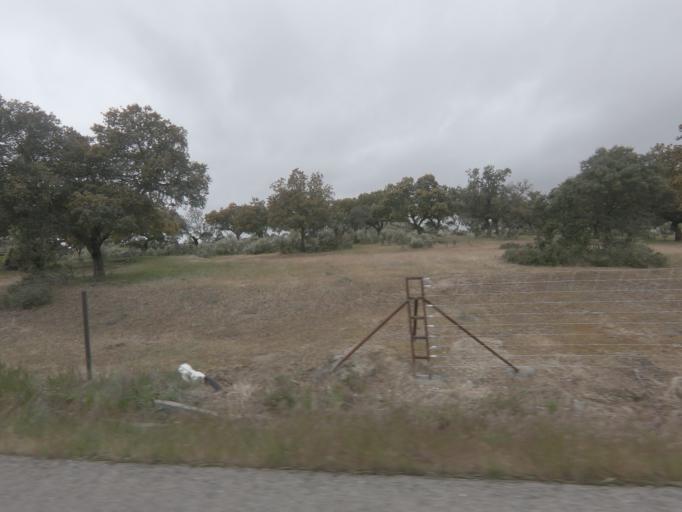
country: ES
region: Extremadura
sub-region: Provincia de Caceres
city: Malpartida de Caceres
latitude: 39.3912
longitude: -6.4305
